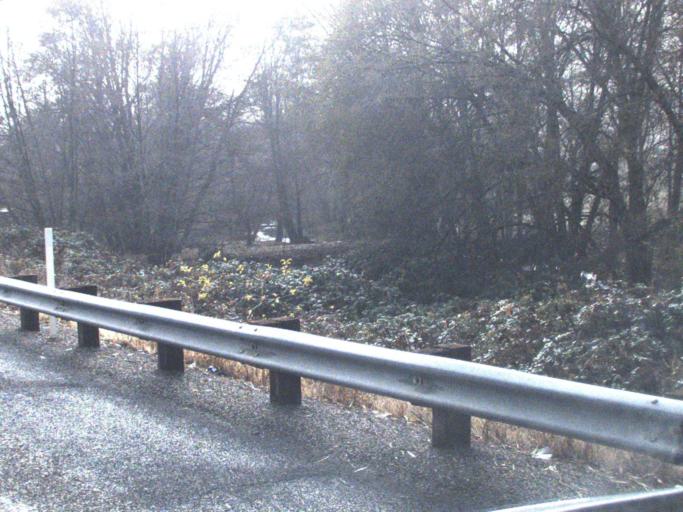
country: US
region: Washington
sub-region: Asotin County
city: Clarkston Heights-Vineland
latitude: 46.4256
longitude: -117.2918
